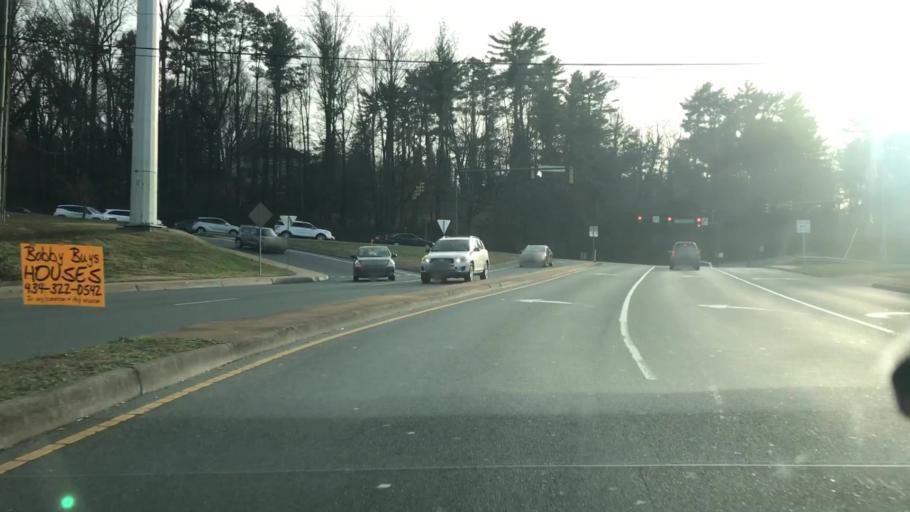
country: US
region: Virginia
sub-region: City of Charlottesville
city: Charlottesville
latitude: 38.0574
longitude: -78.4886
